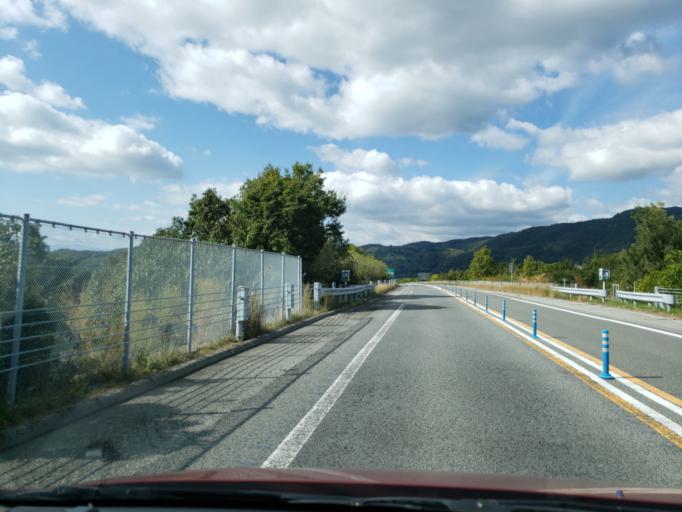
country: JP
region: Tokushima
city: Kamojimacho-jogejima
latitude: 34.1186
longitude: 134.3358
